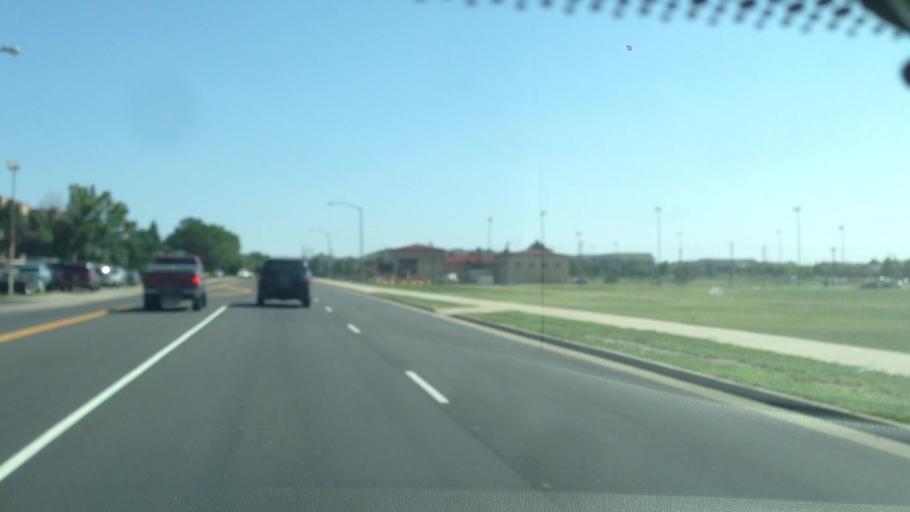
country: US
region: Colorado
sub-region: Adams County
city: Aurora
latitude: 39.7296
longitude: -104.8754
